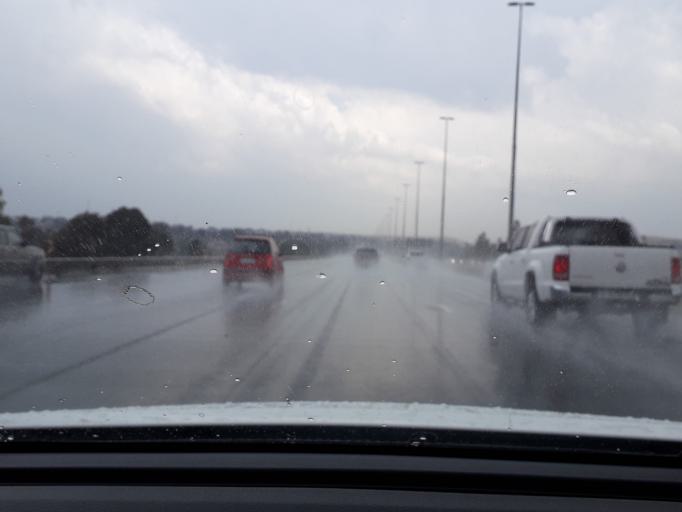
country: ZA
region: Gauteng
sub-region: City of Johannesburg Metropolitan Municipality
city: Roodepoort
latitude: -26.1916
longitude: 27.9493
